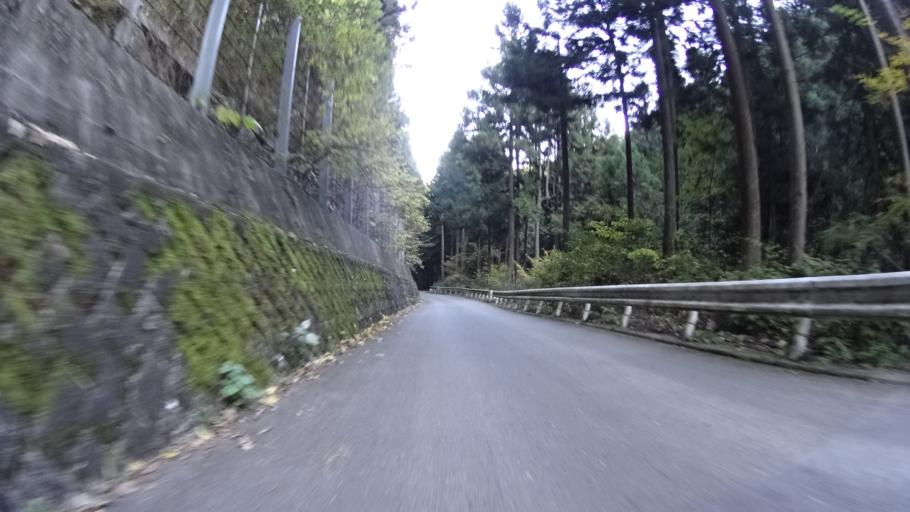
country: JP
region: Yamanashi
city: Uenohara
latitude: 35.6589
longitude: 139.1744
